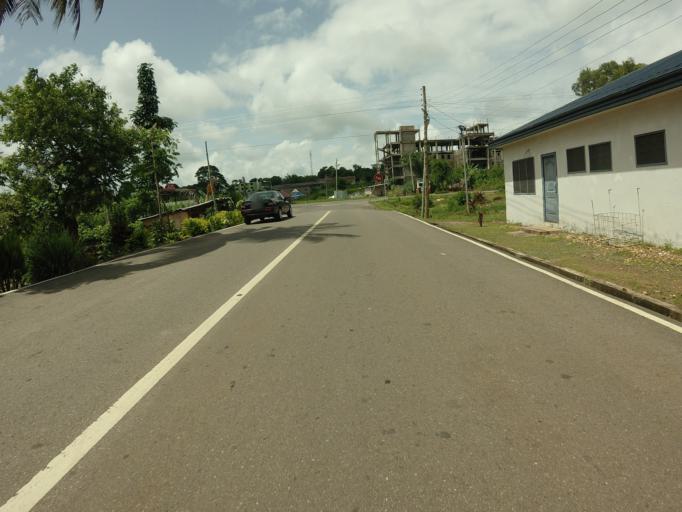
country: GH
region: Volta
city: Ho
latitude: 6.6100
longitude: 0.4578
